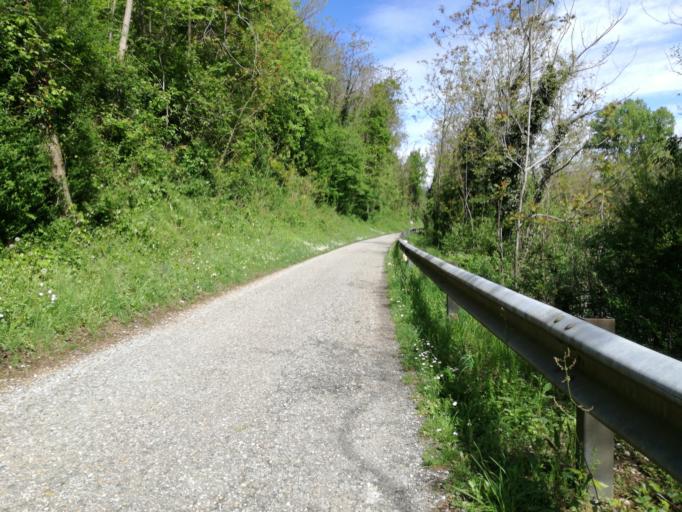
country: IT
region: Lombardy
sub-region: Provincia di Monza e Brianza
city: Porto d'Adda
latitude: 45.6611
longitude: 9.4860
